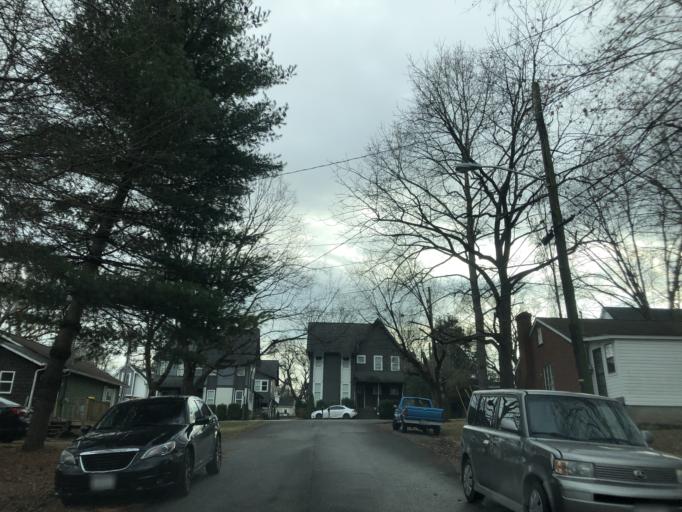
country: US
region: Tennessee
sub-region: Davidson County
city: Nashville
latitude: 36.2017
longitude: -86.7240
